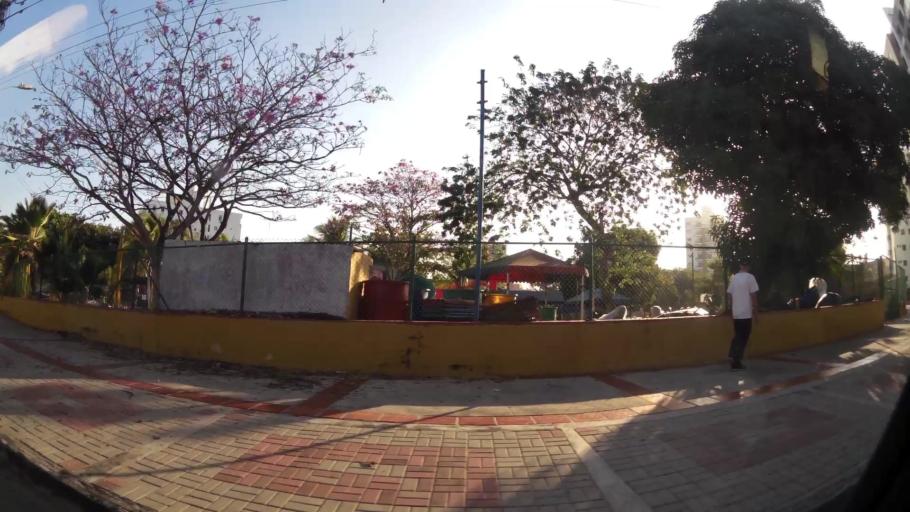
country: CO
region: Atlantico
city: Barranquilla
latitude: 11.0014
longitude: -74.8250
